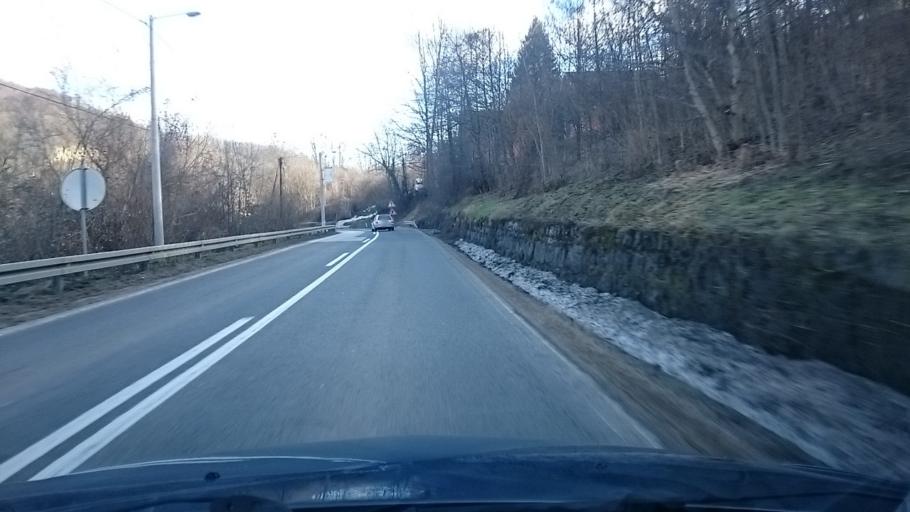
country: BA
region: Republika Srpska
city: Hiseti
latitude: 44.7195
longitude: 17.1612
